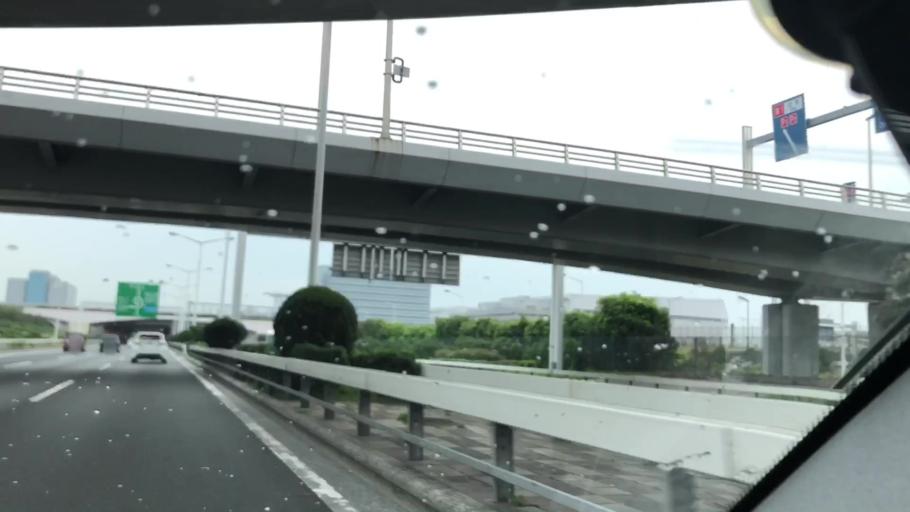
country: JP
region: Kanagawa
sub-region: Kawasaki-shi
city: Kawasaki
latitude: 35.5472
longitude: 139.7884
